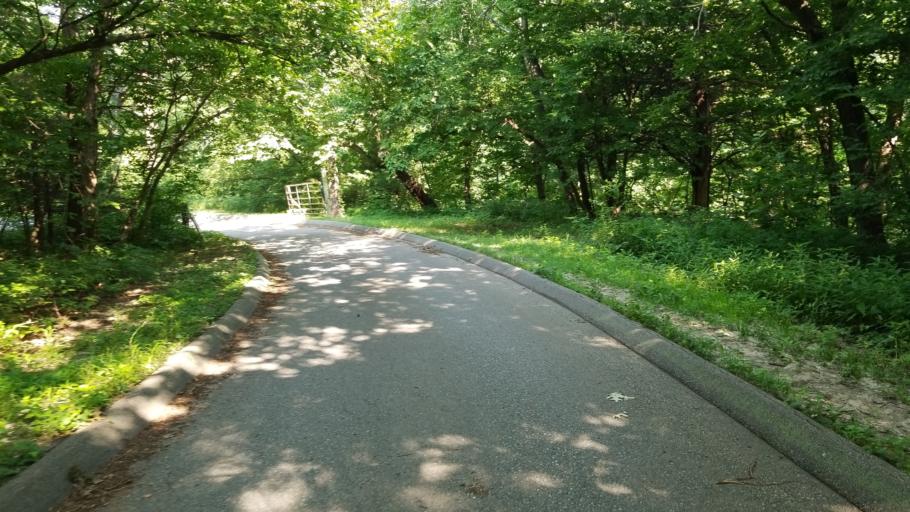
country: US
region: Nebraska
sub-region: Cass County
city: Louisville
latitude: 41.0214
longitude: -96.2456
